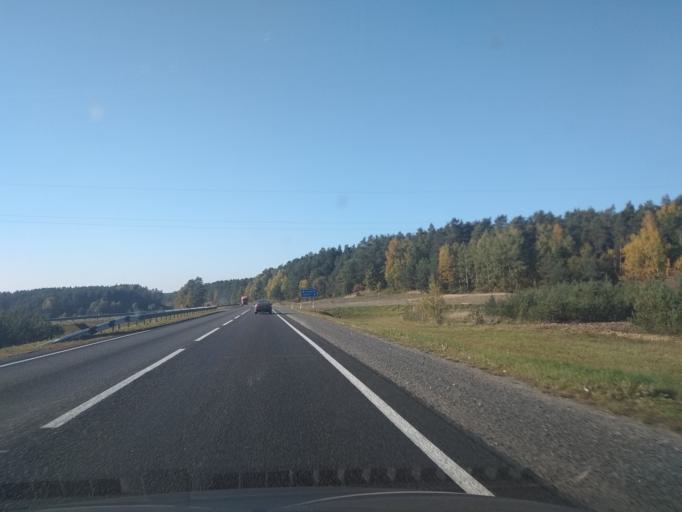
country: BY
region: Grodnenskaya
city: Zhyrovichy
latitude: 53.0509
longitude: 25.3396
